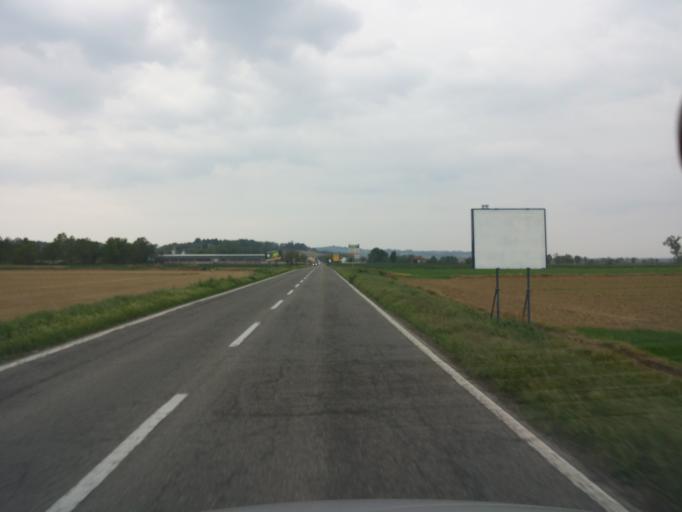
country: IT
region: Piedmont
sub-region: Provincia di Alessandria
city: Terruggia
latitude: 45.0811
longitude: 8.4769
